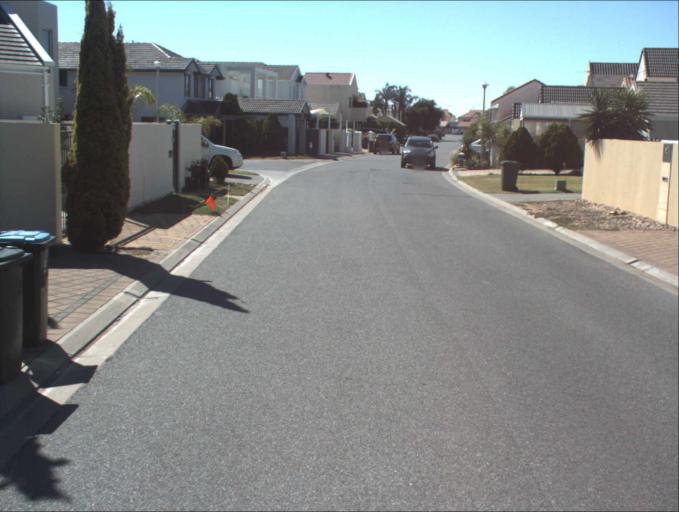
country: AU
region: South Australia
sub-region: Port Adelaide Enfield
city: Birkenhead
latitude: -34.7941
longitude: 138.4885
